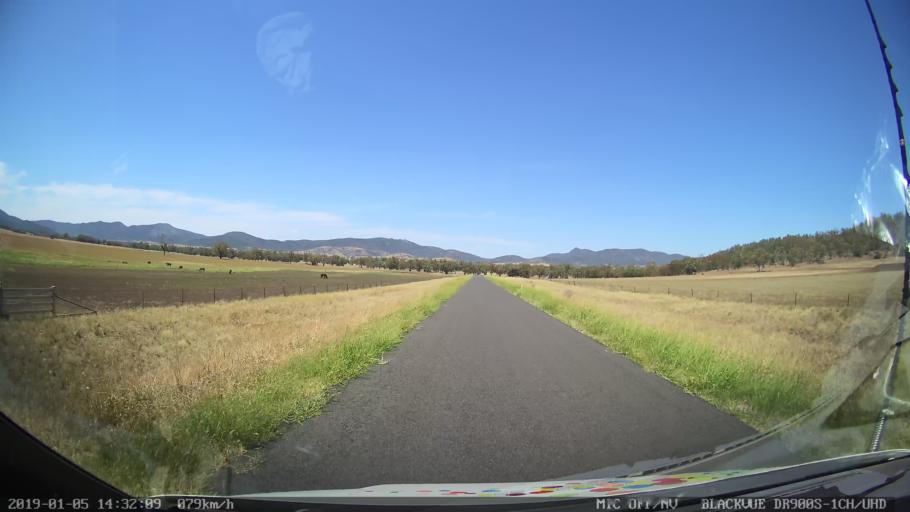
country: AU
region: New South Wales
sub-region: Tamworth Municipality
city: Phillip
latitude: -31.2220
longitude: 150.6146
